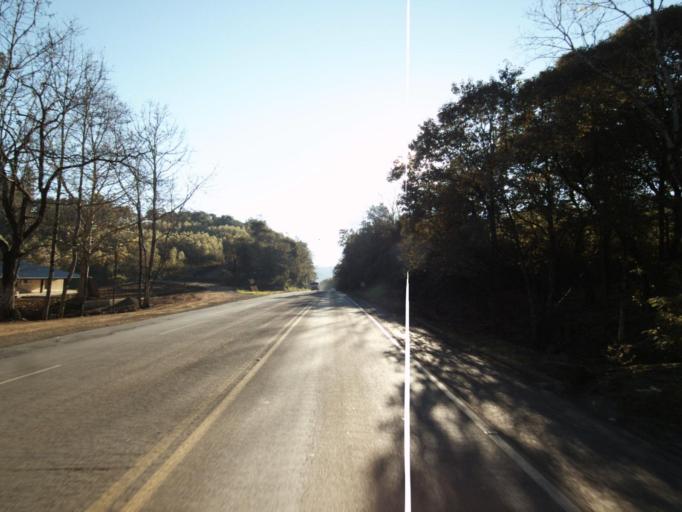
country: BR
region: Santa Catarina
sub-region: Chapeco
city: Chapeco
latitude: -26.9270
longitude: -52.8468
